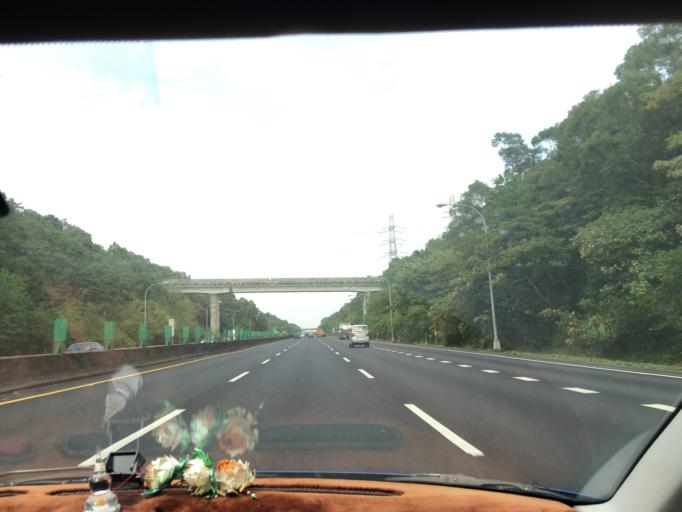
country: TW
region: Taiwan
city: Daxi
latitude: 24.8160
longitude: 121.2005
